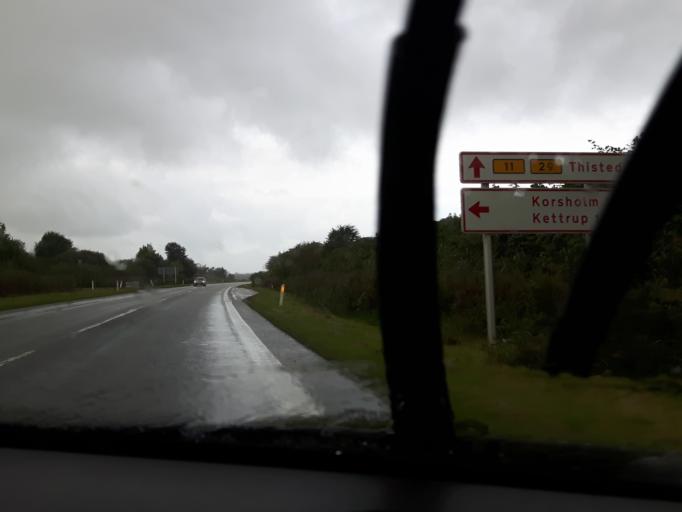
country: DK
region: North Denmark
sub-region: Jammerbugt Kommune
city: Fjerritslev
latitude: 57.0748
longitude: 9.2551
